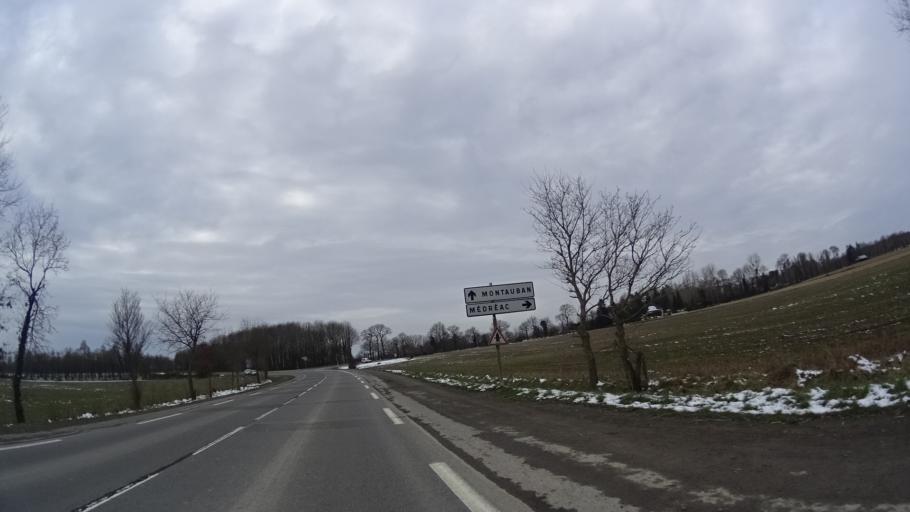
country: FR
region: Brittany
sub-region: Departement d'Ille-et-Vilaine
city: Montauban-de-Bretagne
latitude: 48.2092
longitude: -2.0425
